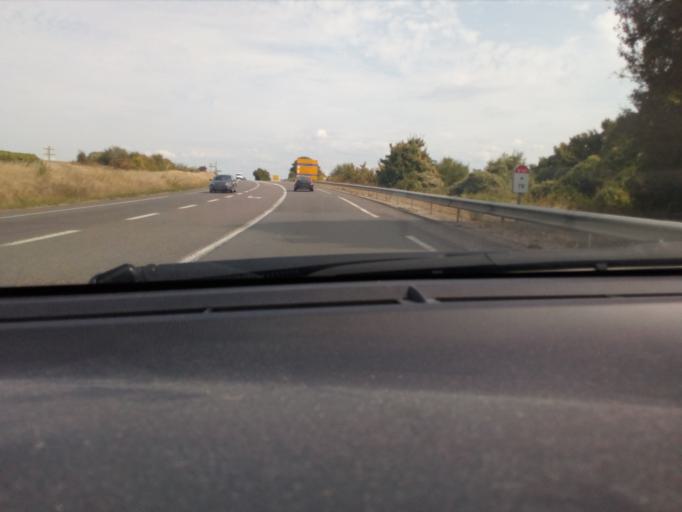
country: FR
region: Poitou-Charentes
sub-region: Departement de la Charente
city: Hiersac
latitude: 45.6711
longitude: 0.0216
